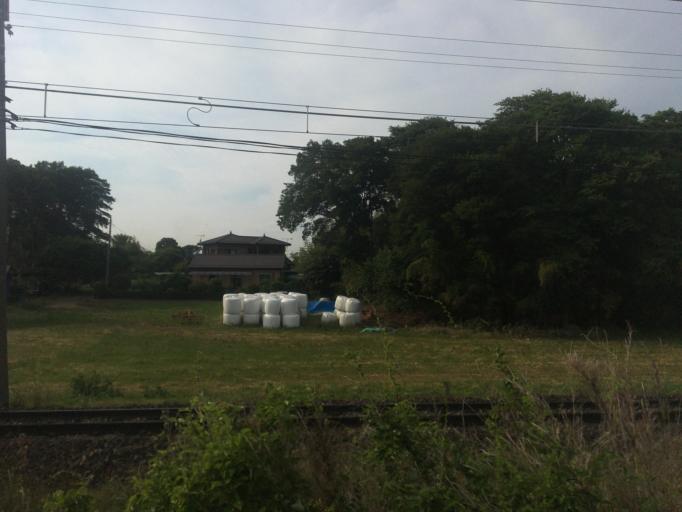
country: JP
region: Saitama
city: Fukayacho
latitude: 36.1427
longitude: 139.2944
